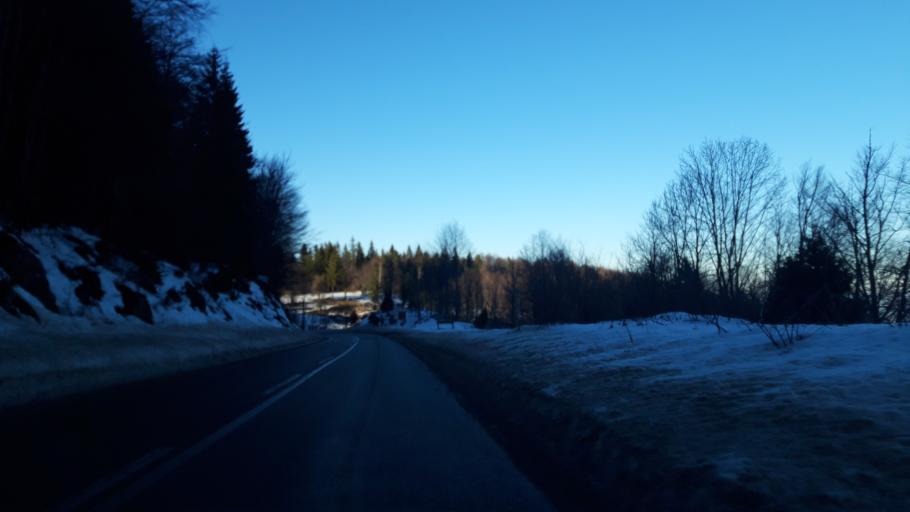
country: BA
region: Republika Srpska
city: Vlasenica
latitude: 44.1435
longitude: 18.9442
